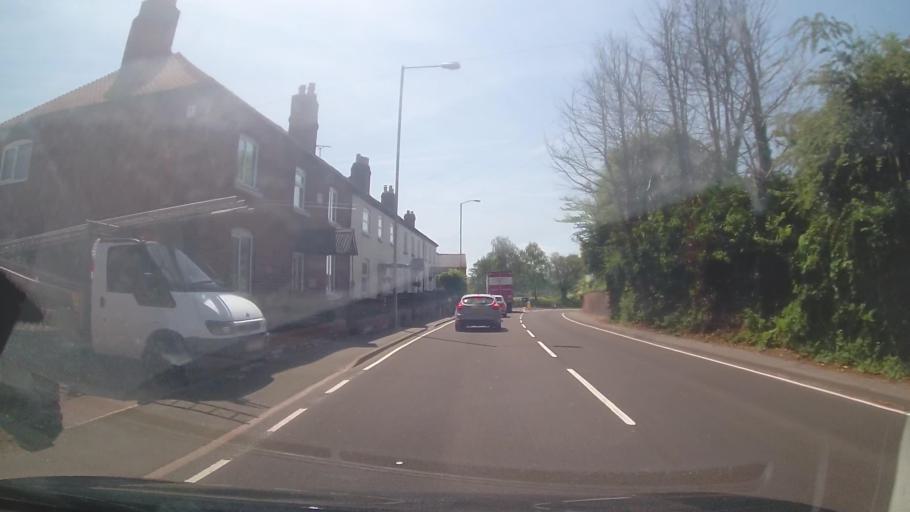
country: GB
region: England
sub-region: Herefordshire
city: Hereford
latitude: 52.0762
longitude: -2.7219
